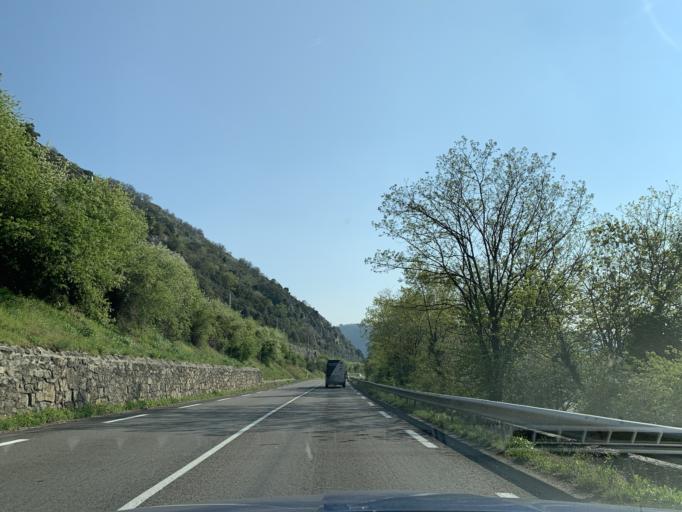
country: FR
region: Rhone-Alpes
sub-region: Departement de l'Ardeche
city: Saint-Jean-de-Muzols
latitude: 45.0871
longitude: 4.8331
